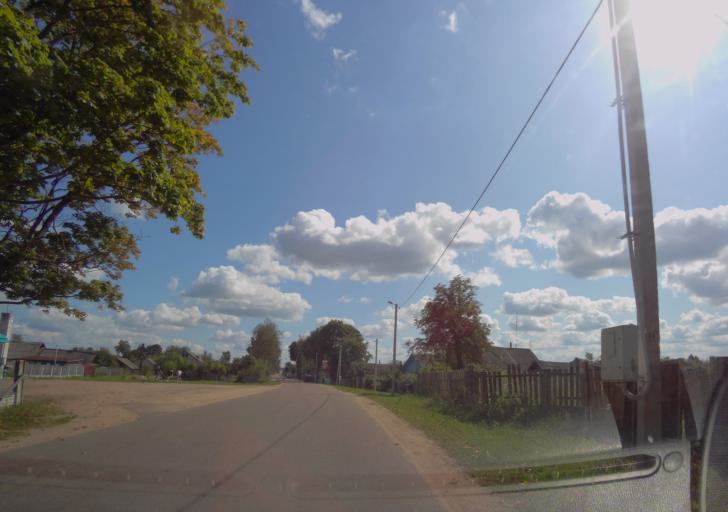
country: BY
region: Minsk
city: Horad Barysaw
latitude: 54.3864
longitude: 28.4725
